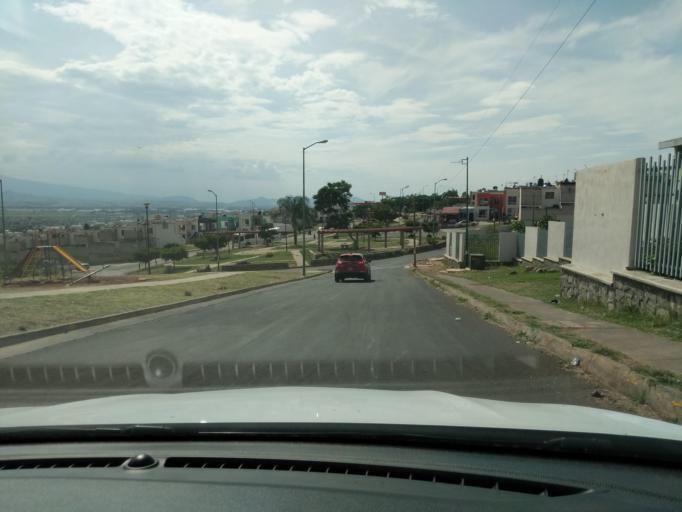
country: MX
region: Jalisco
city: San Jose del Castillo
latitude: 20.5213
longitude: -103.2284
